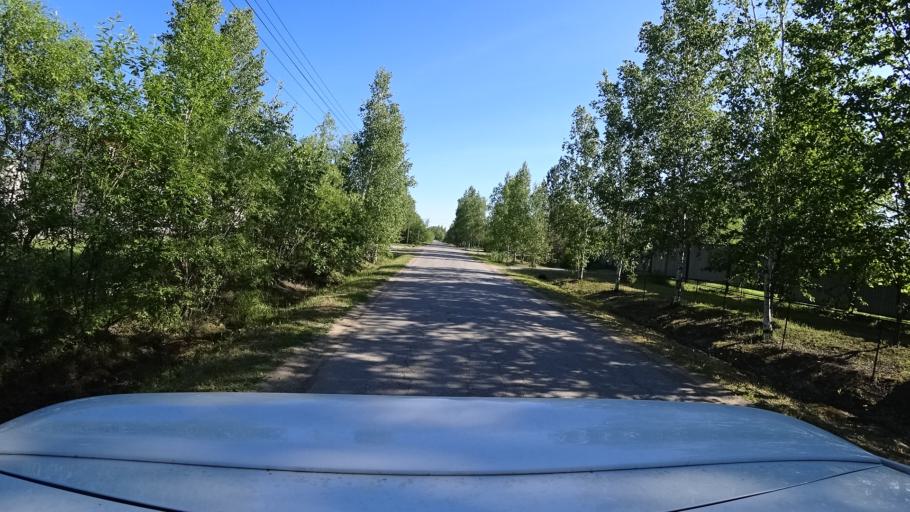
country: RU
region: Khabarovsk Krai
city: Topolevo
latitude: 48.5495
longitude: 135.1744
